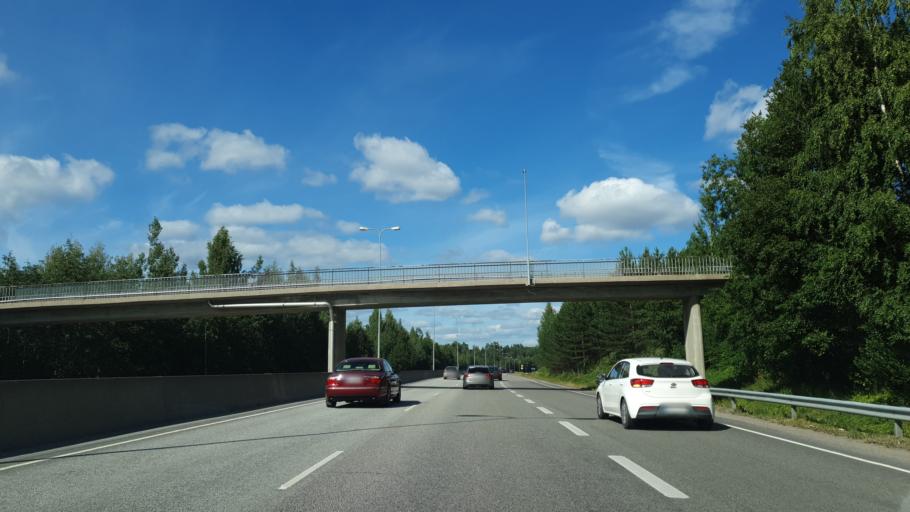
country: FI
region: Central Finland
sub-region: Jyvaeskylae
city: Jyvaeskylae
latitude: 62.2201
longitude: 25.7251
